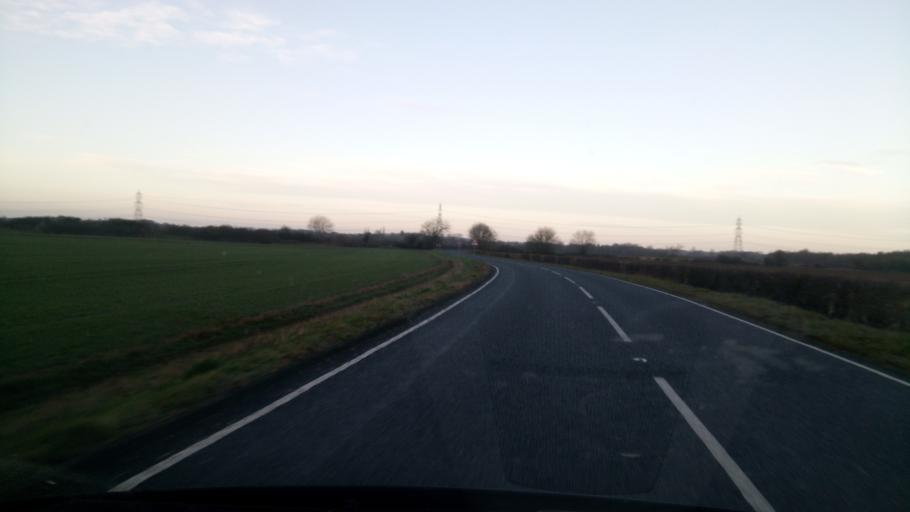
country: GB
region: England
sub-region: Peterborough
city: Upton
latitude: 52.5764
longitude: -0.3634
